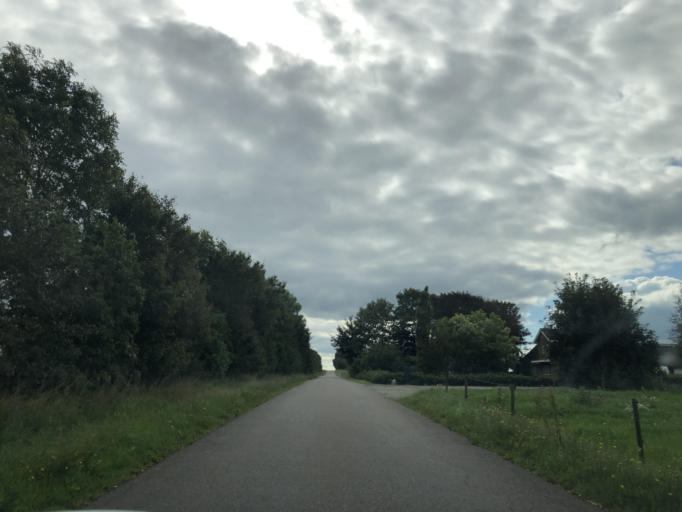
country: DK
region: North Denmark
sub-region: Vesthimmerland Kommune
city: Aars
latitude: 56.8318
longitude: 9.6597
